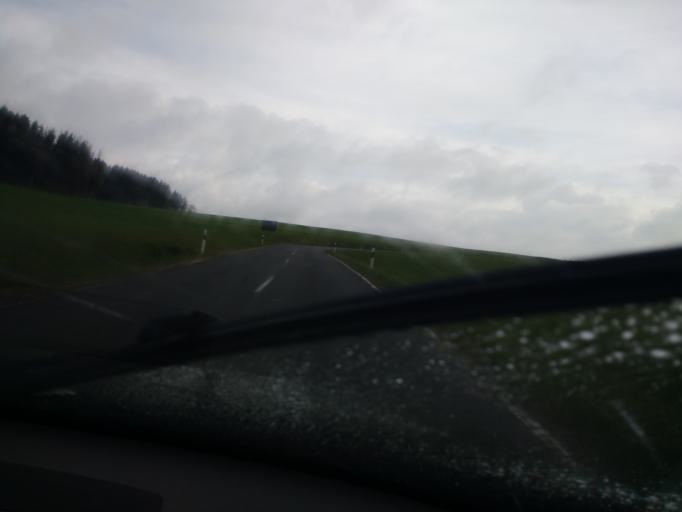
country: DE
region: Rheinland-Pfalz
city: Kalenborn-Scheuern
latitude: 50.2483
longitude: 6.5862
